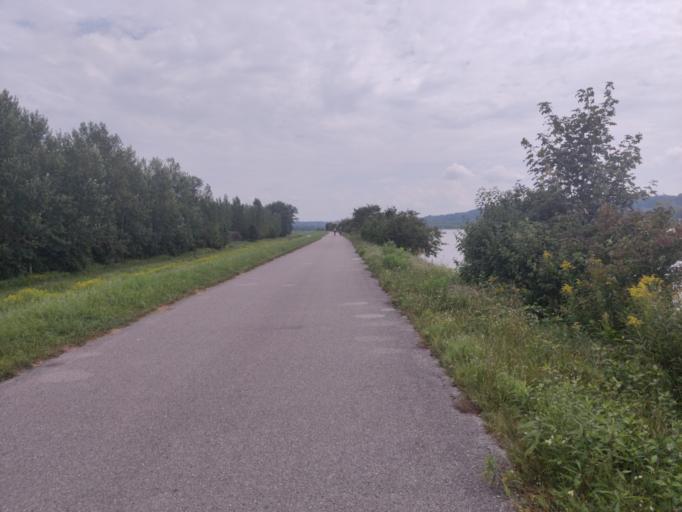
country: AT
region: Lower Austria
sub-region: Politischer Bezirk Amstetten
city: Strengberg
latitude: 48.1729
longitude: 14.6512
